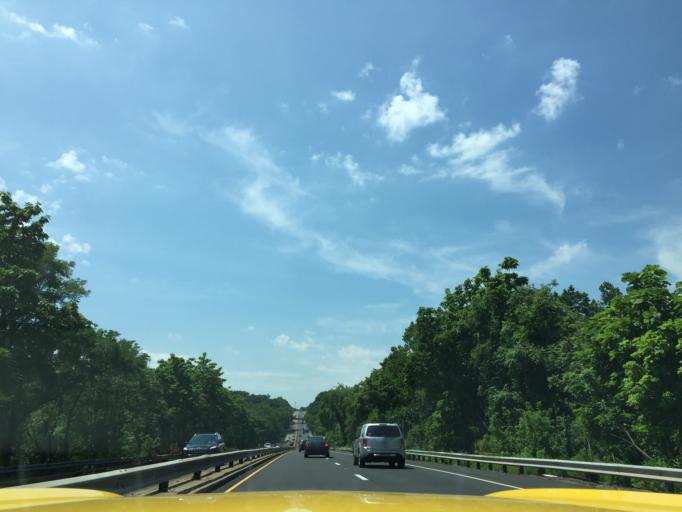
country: US
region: Pennsylvania
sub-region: Bucks County
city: Trevose
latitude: 40.1498
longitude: -74.9499
